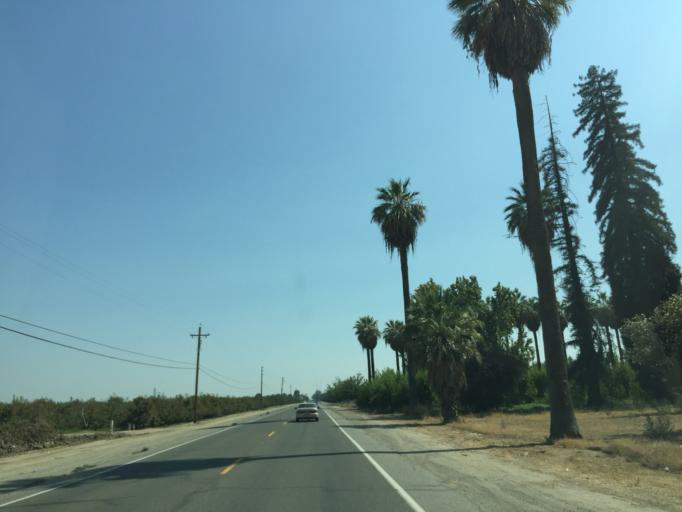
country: US
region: California
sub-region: Kings County
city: Lucerne
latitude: 36.3814
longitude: -119.6731
